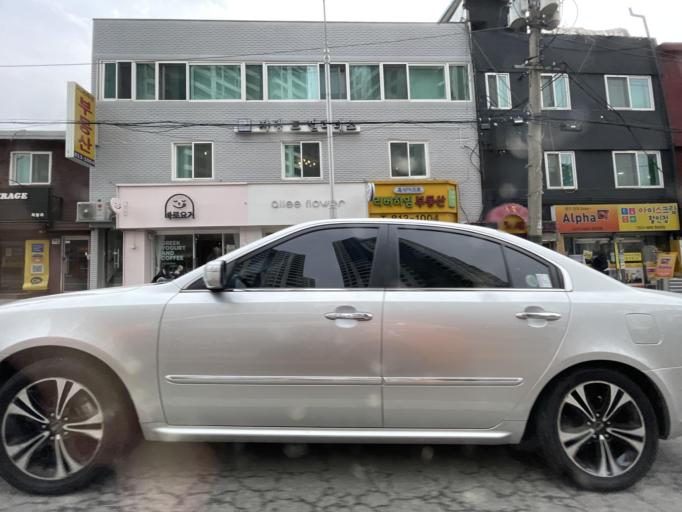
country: KR
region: Seoul
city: Seoul
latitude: 37.5091
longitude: 126.9621
